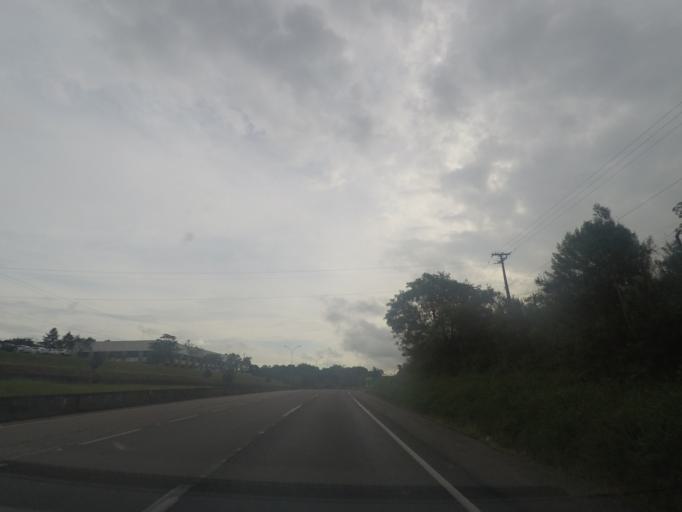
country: BR
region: Parana
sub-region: Quatro Barras
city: Quatro Barras
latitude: -25.3467
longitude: -49.0468
